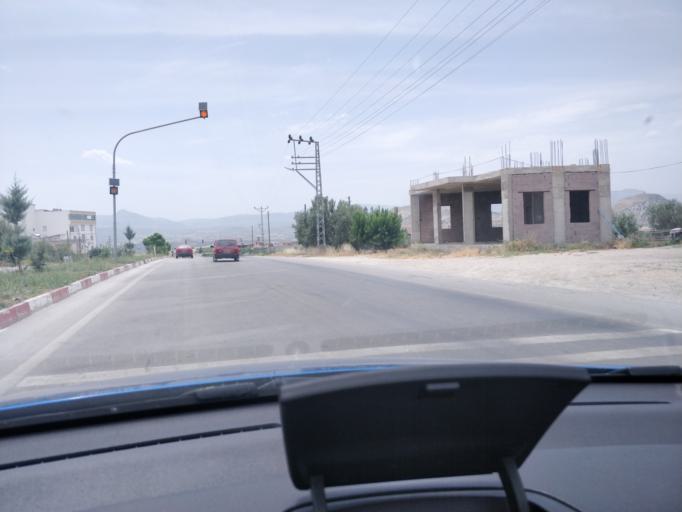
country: TR
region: Mersin
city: Mut
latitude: 36.6096
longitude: 33.4388
